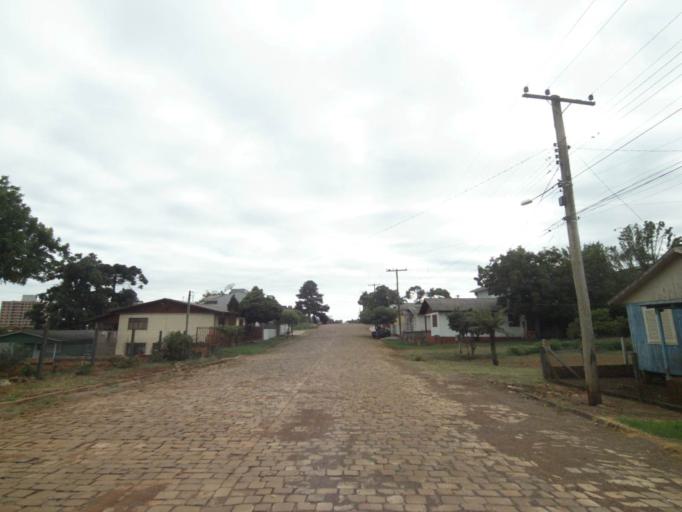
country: BR
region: Rio Grande do Sul
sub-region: Lagoa Vermelha
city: Lagoa Vermelha
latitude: -28.2170
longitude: -51.5157
